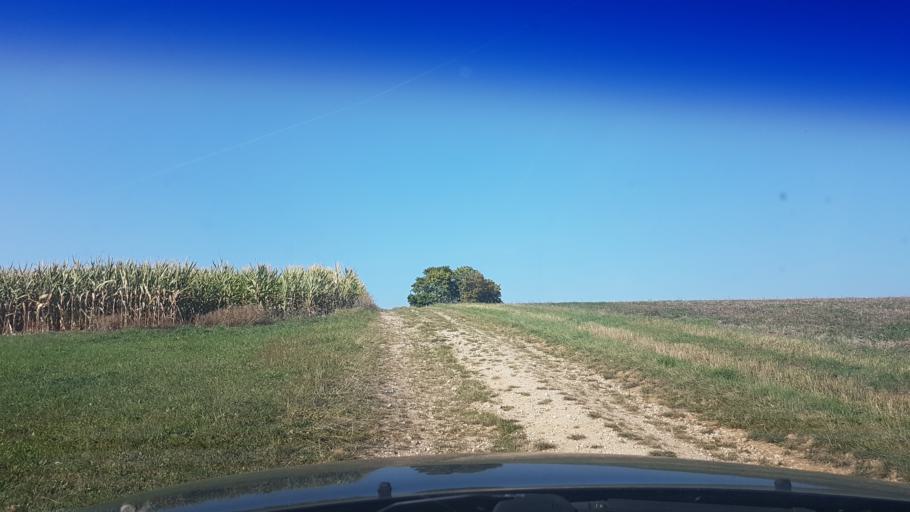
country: DE
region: Bavaria
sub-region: Upper Franconia
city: Memmelsdorf
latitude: 49.9696
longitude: 10.9614
